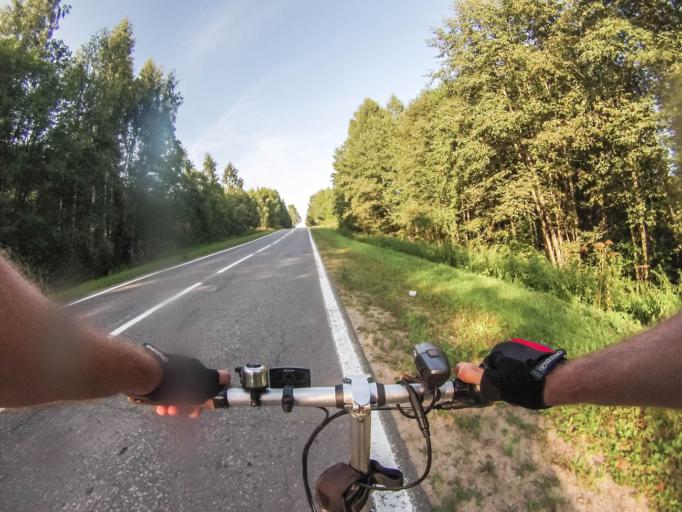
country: RU
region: Jaroslavl
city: Myshkin
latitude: 57.7237
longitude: 38.4164
